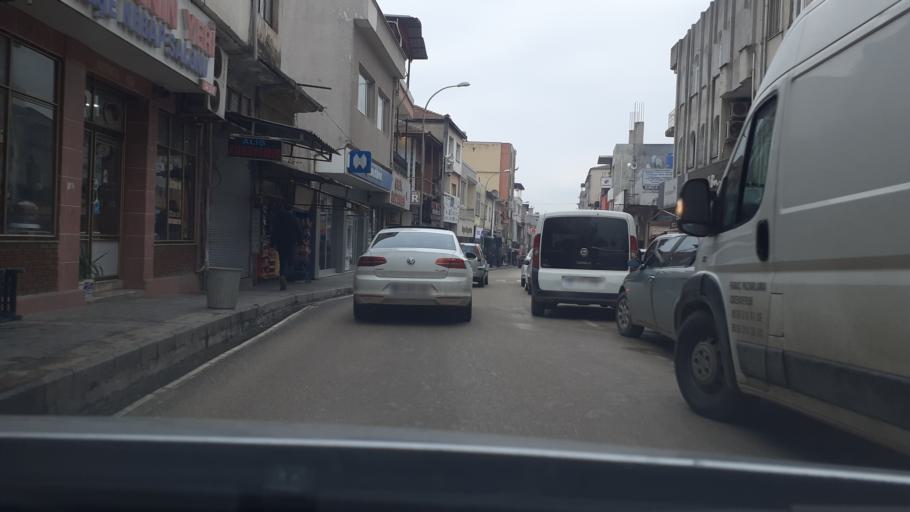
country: TR
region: Hatay
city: Kirikhan
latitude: 36.4991
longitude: 36.3536
